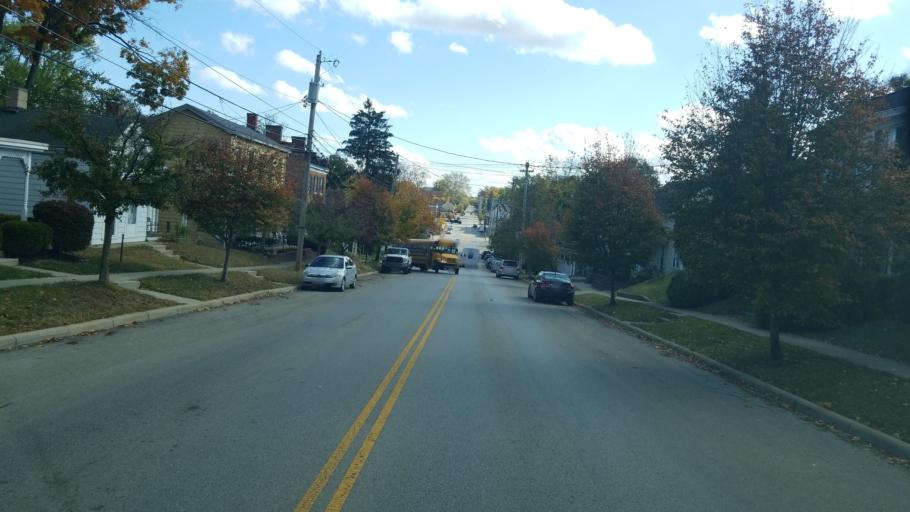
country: US
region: Ohio
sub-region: Warren County
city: Lebanon
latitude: 39.4358
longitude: -84.2121
